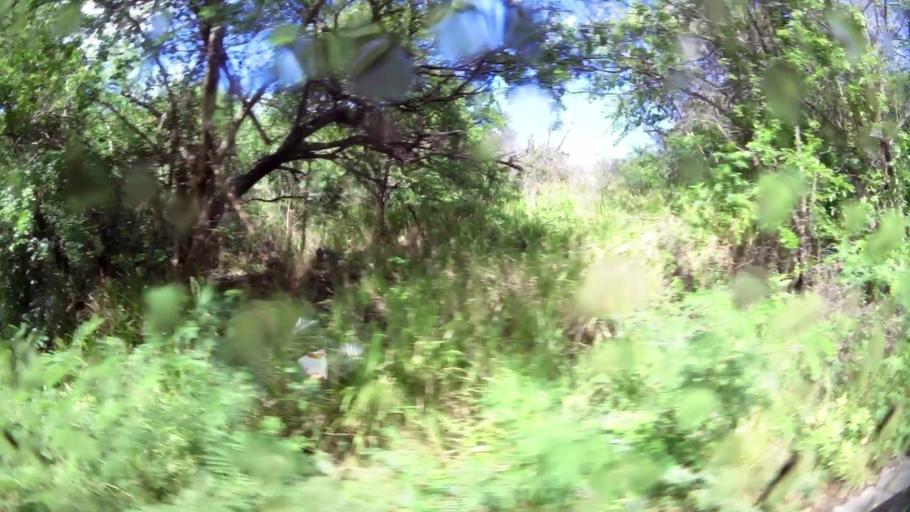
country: MS
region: Saint Peter
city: Saint Peters
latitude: 16.7454
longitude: -62.2292
